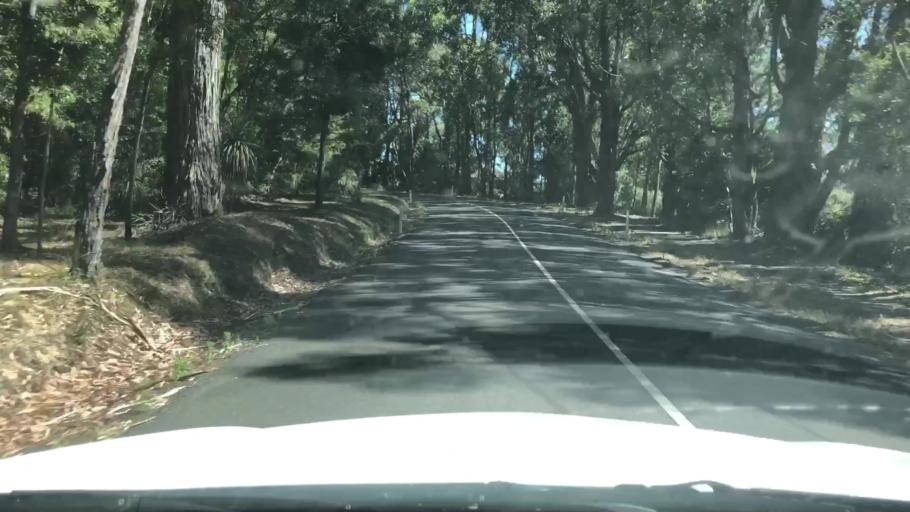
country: AU
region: Victoria
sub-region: Yarra Ranges
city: Macclesfield
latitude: -37.8921
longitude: 145.4754
